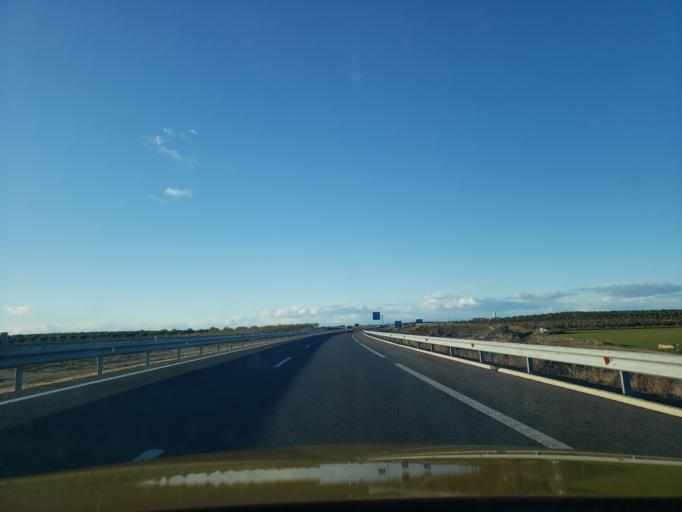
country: ES
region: Castille-La Mancha
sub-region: Province of Toledo
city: Nambroca
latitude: 39.8048
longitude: -3.9679
